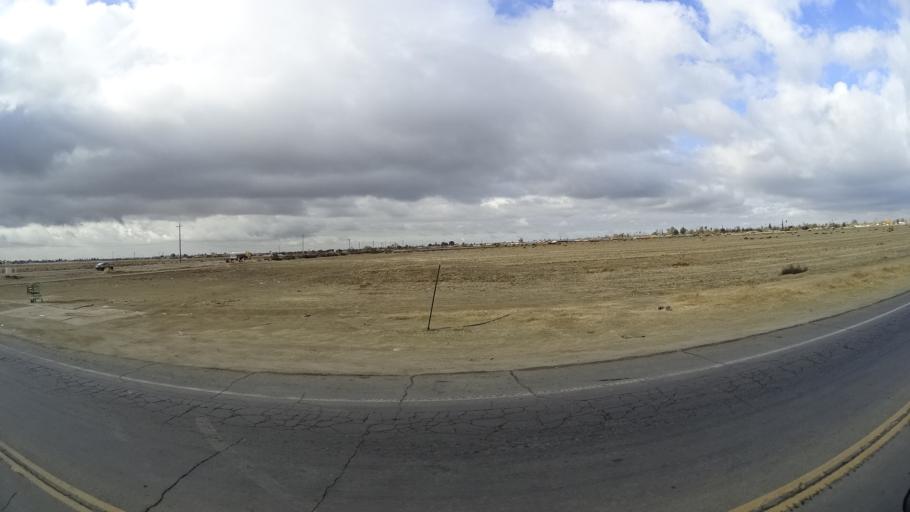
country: US
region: California
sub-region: Kern County
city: Greenfield
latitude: 35.2964
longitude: -118.9854
